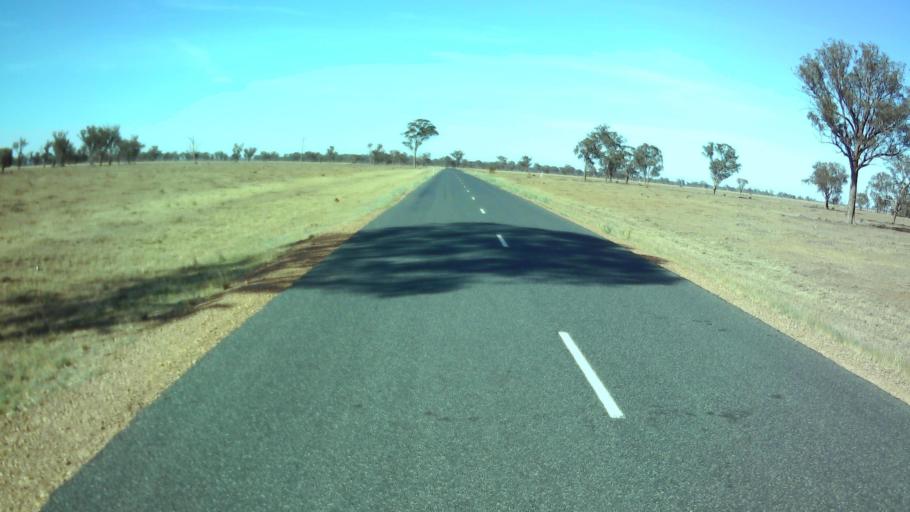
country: AU
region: New South Wales
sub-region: Weddin
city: Grenfell
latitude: -34.0469
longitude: 147.9233
